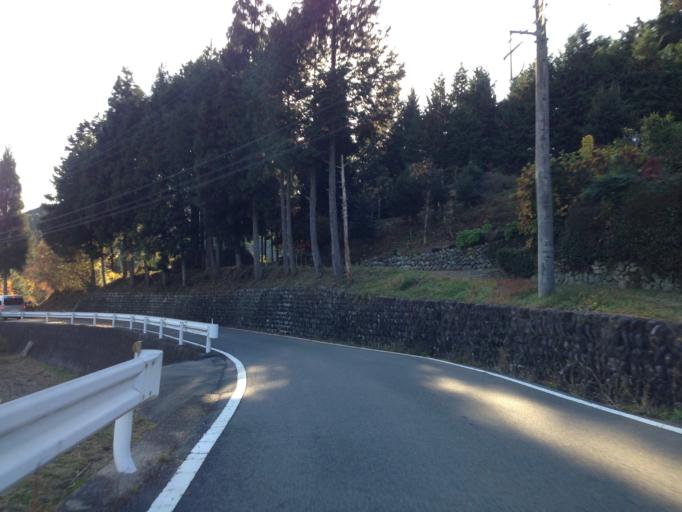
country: JP
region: Gifu
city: Mitake
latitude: 35.6062
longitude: 137.2014
